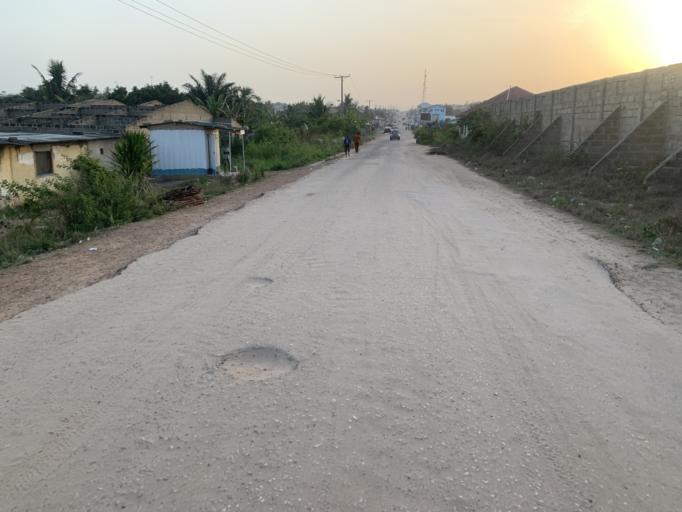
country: GH
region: Central
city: Winneba
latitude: 5.3575
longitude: -0.6088
